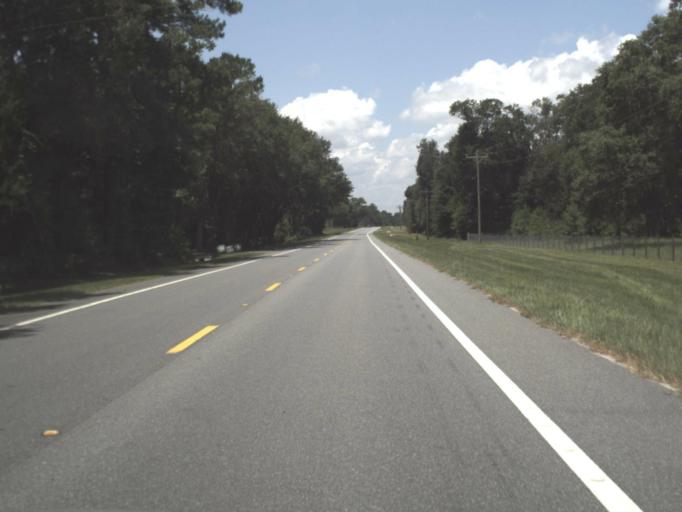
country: US
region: Florida
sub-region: Union County
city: Lake Butler
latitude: 30.0044
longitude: -82.4935
